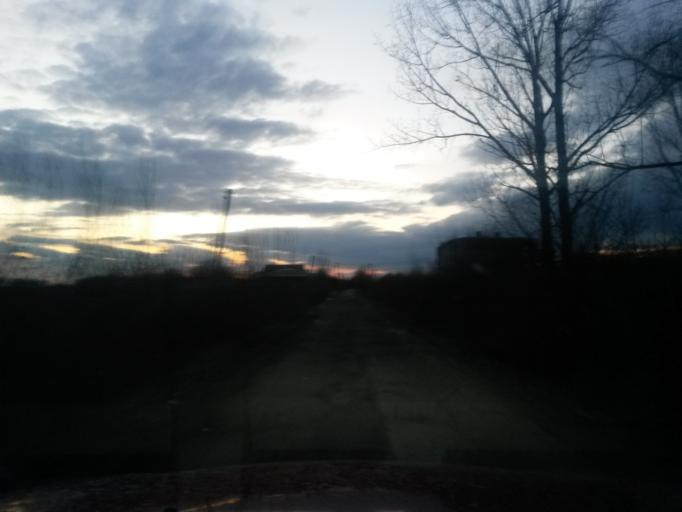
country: SK
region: Kosicky
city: Vinne
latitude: 48.6951
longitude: 22.0446
